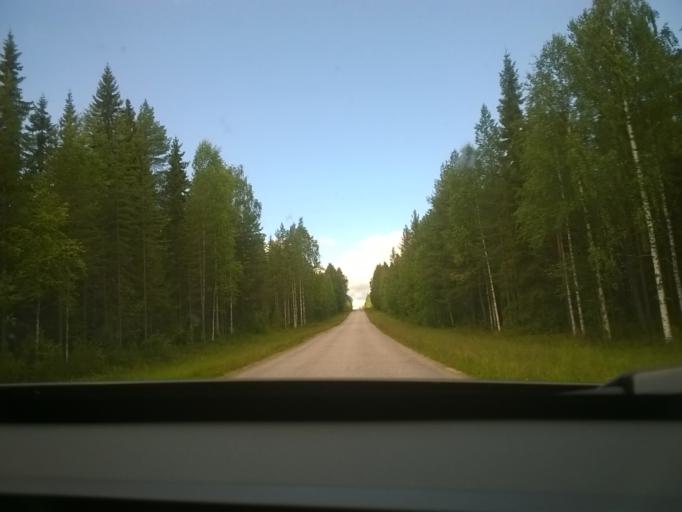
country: FI
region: Kainuu
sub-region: Kehys-Kainuu
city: Kuhmo
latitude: 64.4525
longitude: 29.6630
